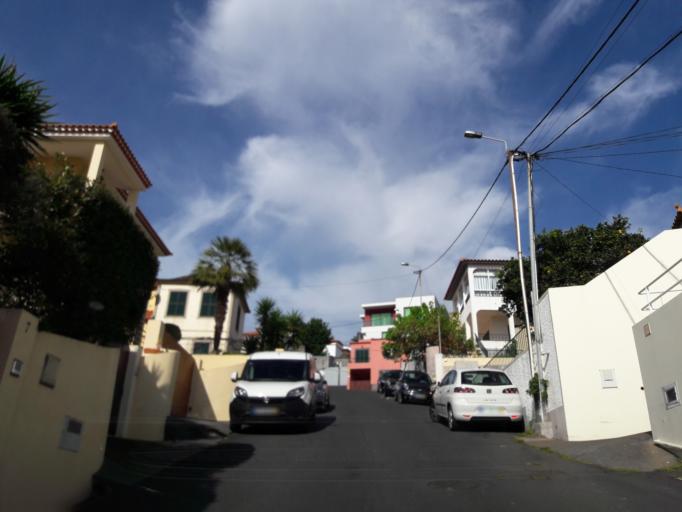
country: PT
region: Madeira
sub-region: Funchal
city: Nossa Senhora do Monte
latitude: 32.6653
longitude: -16.9233
